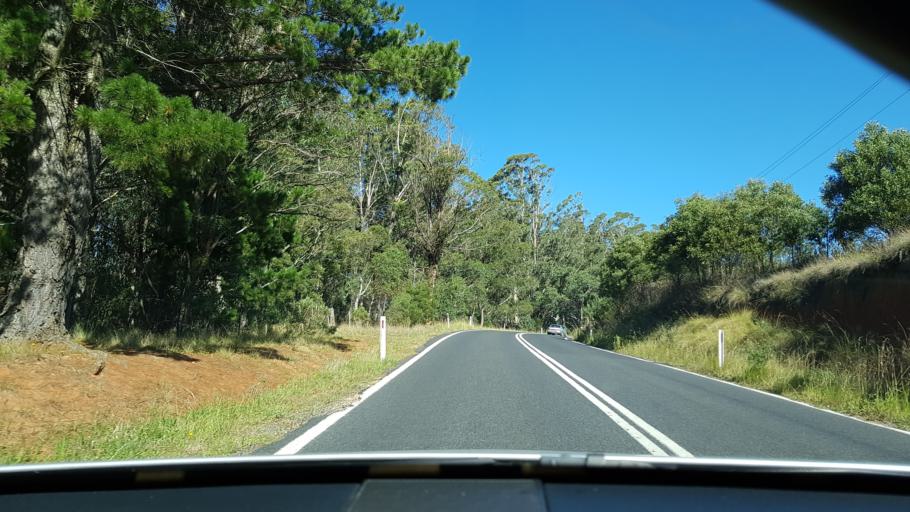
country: AU
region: New South Wales
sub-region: Lithgow
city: Bowenfels
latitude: -33.6736
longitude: 150.0505
